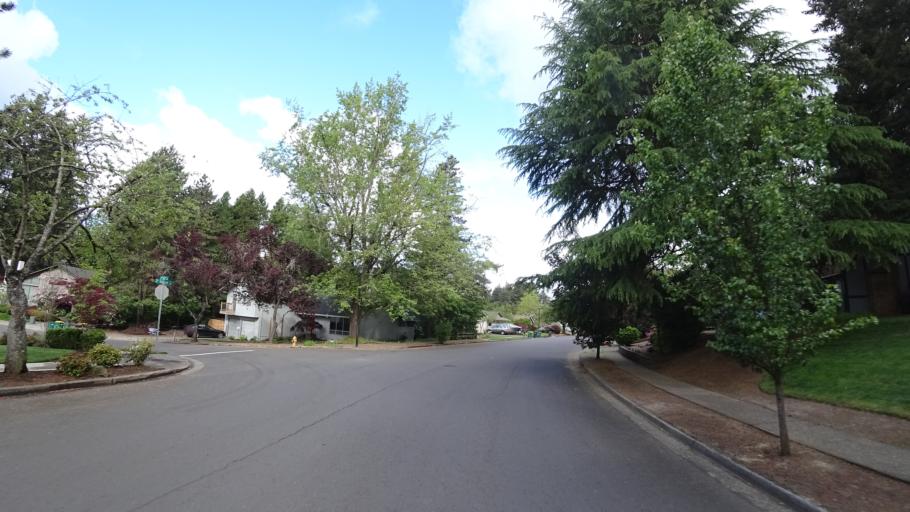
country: US
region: Oregon
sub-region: Washington County
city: Beaverton
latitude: 45.4685
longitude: -122.8231
